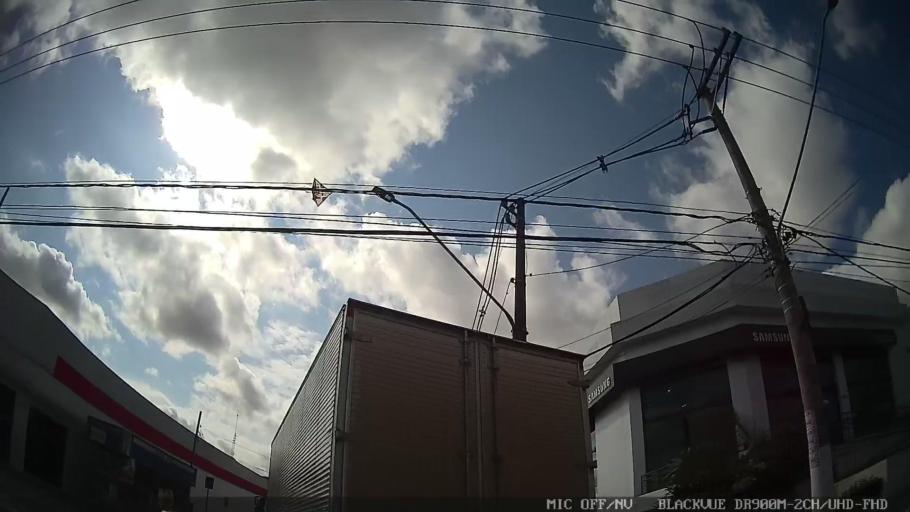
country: BR
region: Sao Paulo
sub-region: Guarulhos
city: Guarulhos
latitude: -23.5003
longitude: -46.4697
